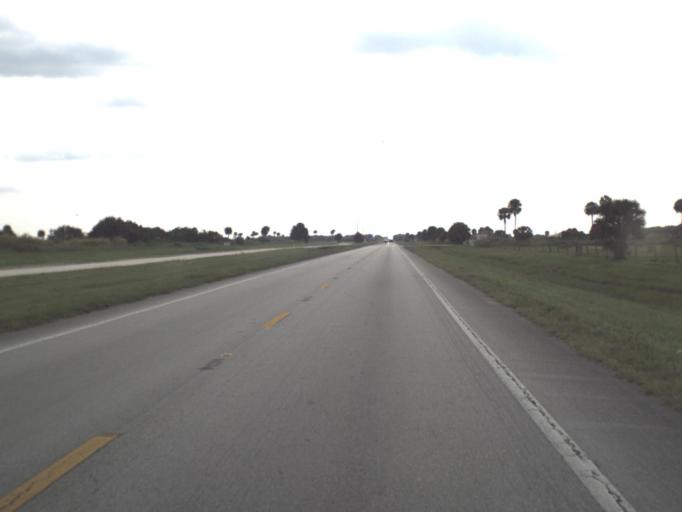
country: US
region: Florida
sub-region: Okeechobee County
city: Cypress Quarters
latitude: 27.4194
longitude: -80.8132
